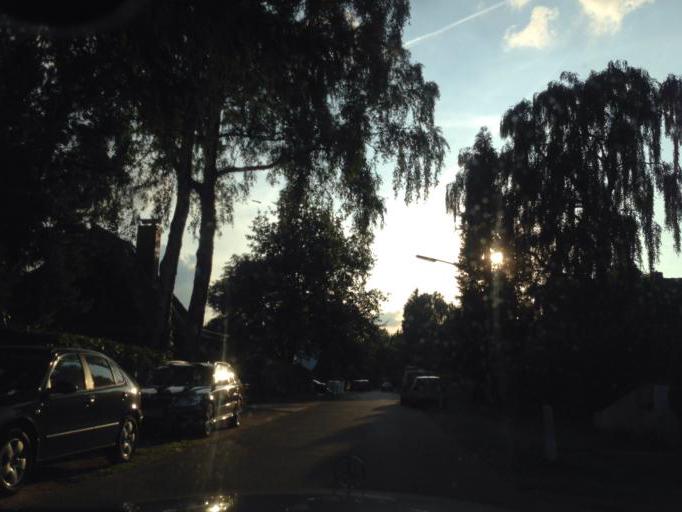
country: DE
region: Hamburg
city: Wandsbek
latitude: 53.5700
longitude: 10.1177
